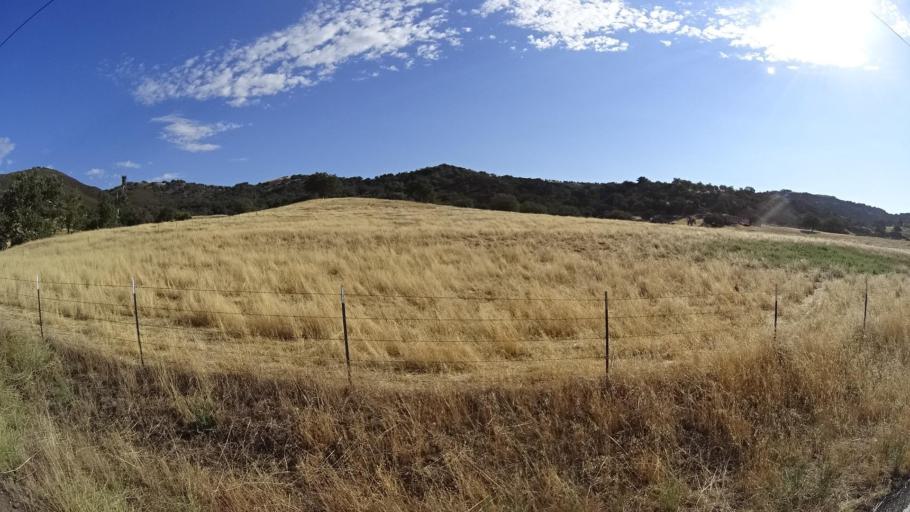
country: US
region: California
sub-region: San Diego County
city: Julian
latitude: 33.1458
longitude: -116.6907
